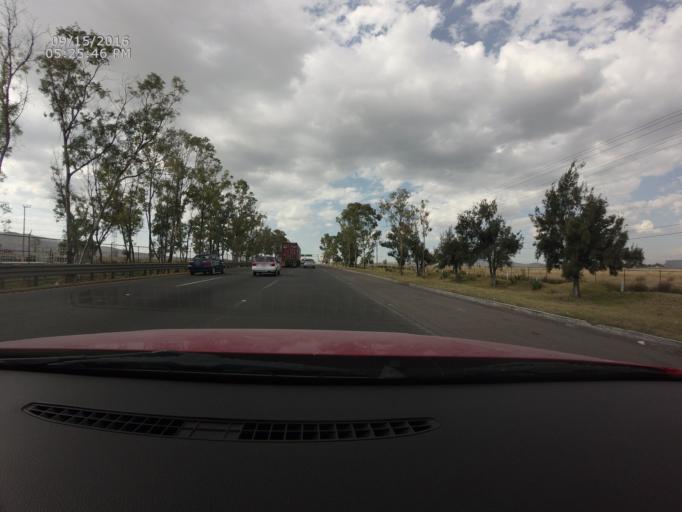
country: MX
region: Mexico
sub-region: Cuautitlan
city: San Jose del Puente
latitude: 19.7322
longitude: -99.2103
